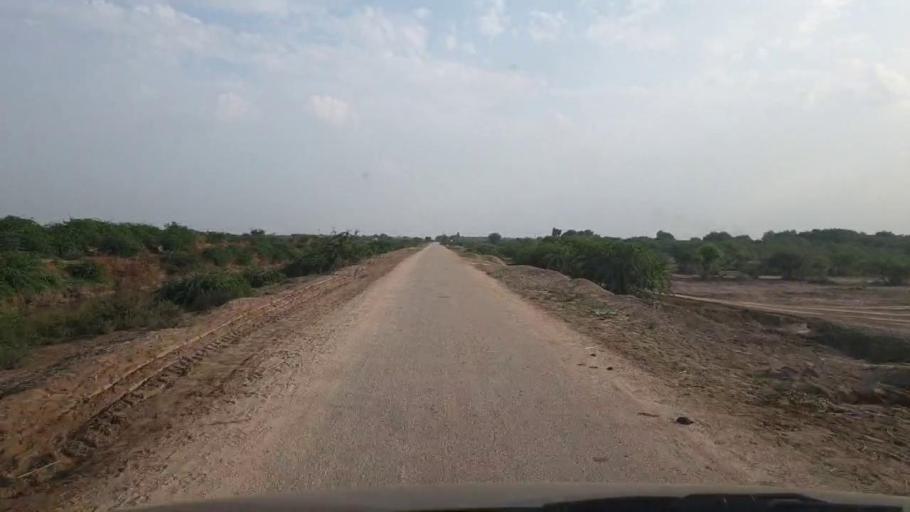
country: PK
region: Sindh
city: Badin
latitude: 24.5339
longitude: 68.6770
